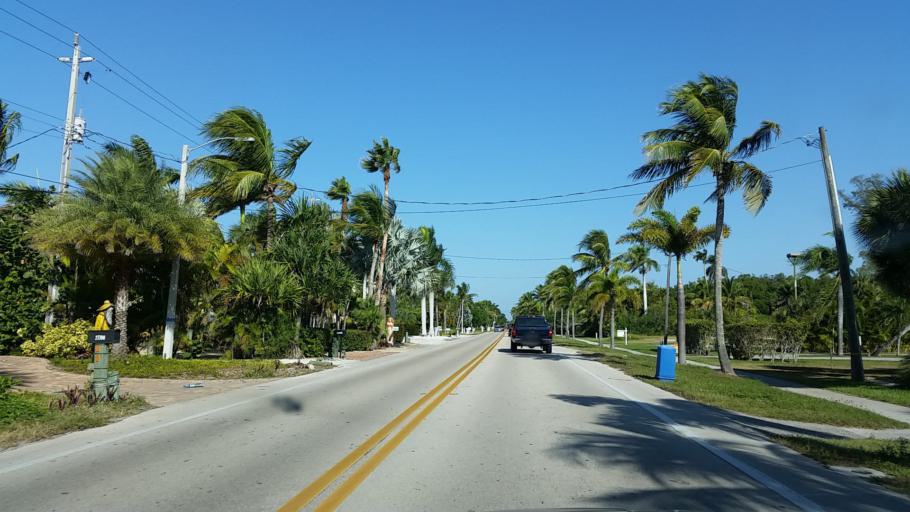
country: US
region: Florida
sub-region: Lee County
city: Bonita Springs
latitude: 26.3351
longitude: -81.8468
